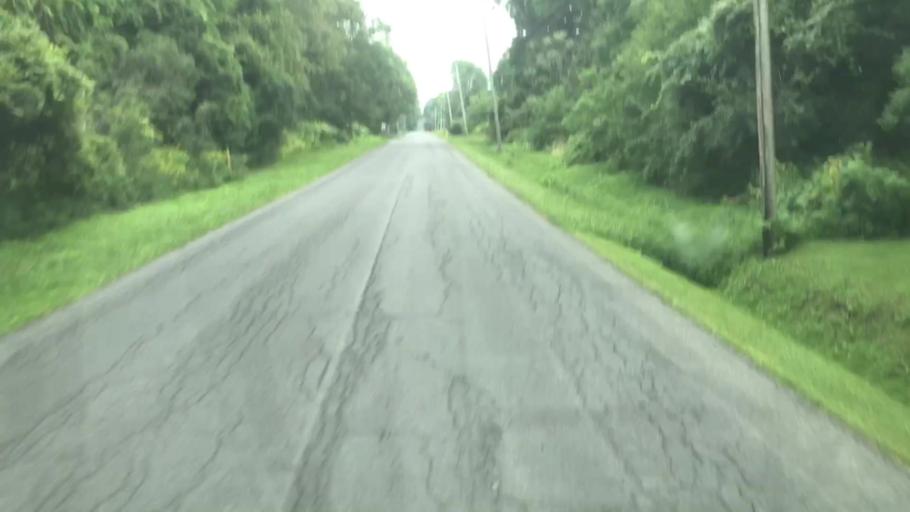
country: US
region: New York
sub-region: Onondaga County
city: Skaneateles
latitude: 42.9525
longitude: -76.4514
